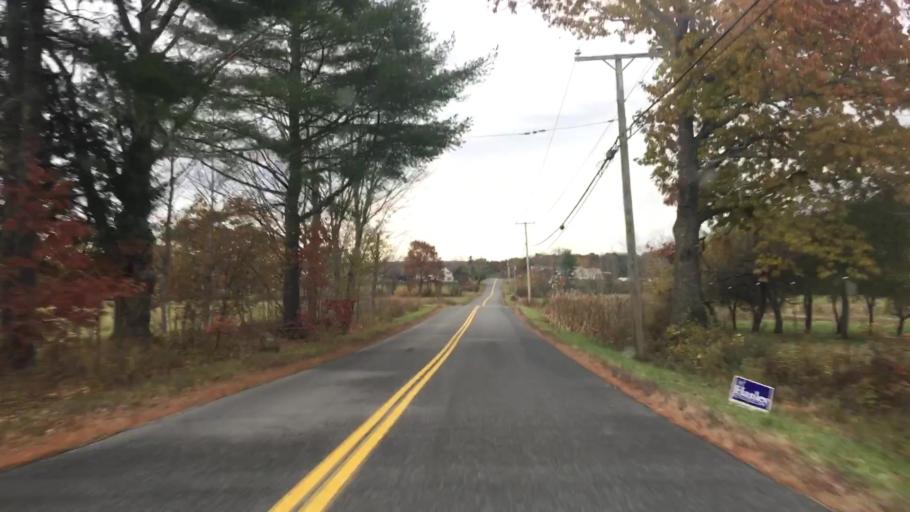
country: US
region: Maine
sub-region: Kennebec County
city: Pittston
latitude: 44.1711
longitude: -69.7246
